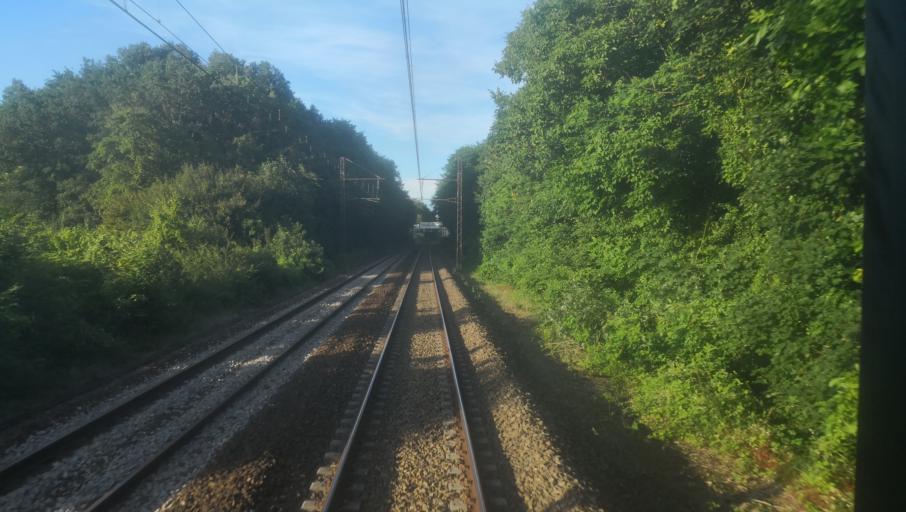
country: FR
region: Centre
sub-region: Departement de l'Indre
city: Montierchaume
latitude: 46.8408
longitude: 1.7717
